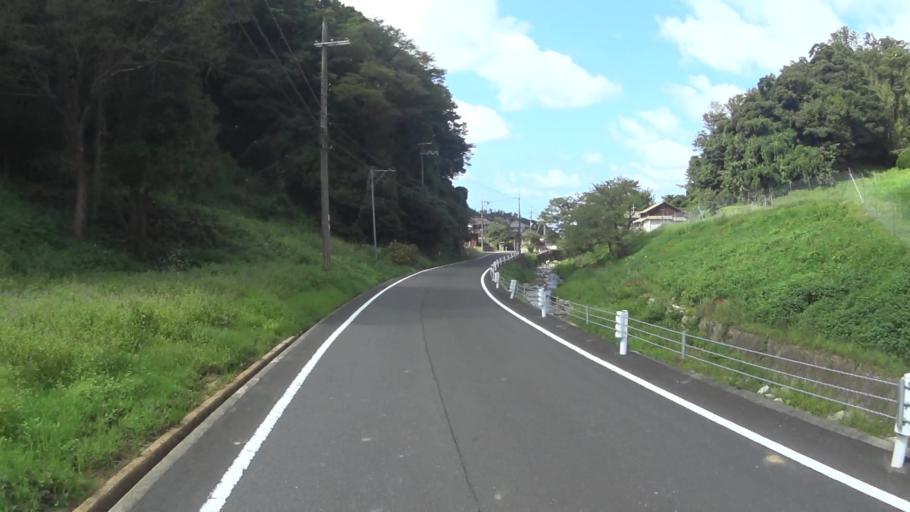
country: JP
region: Kyoto
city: Miyazu
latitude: 35.7452
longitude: 135.1798
